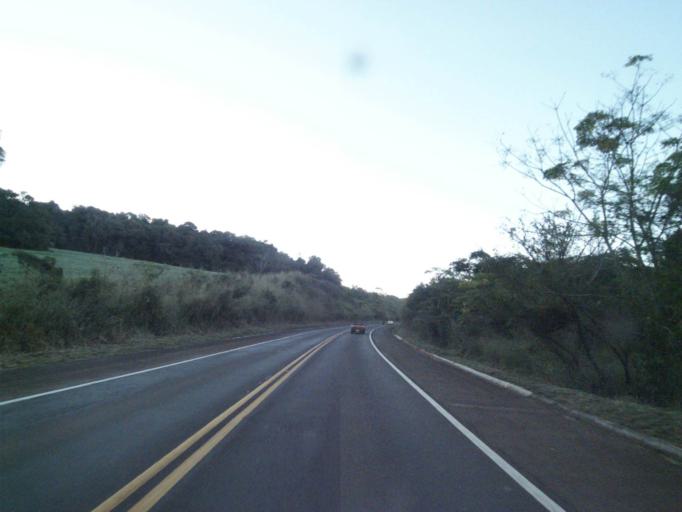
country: BR
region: Parana
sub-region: Londrina
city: Londrina
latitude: -23.5700
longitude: -51.1192
